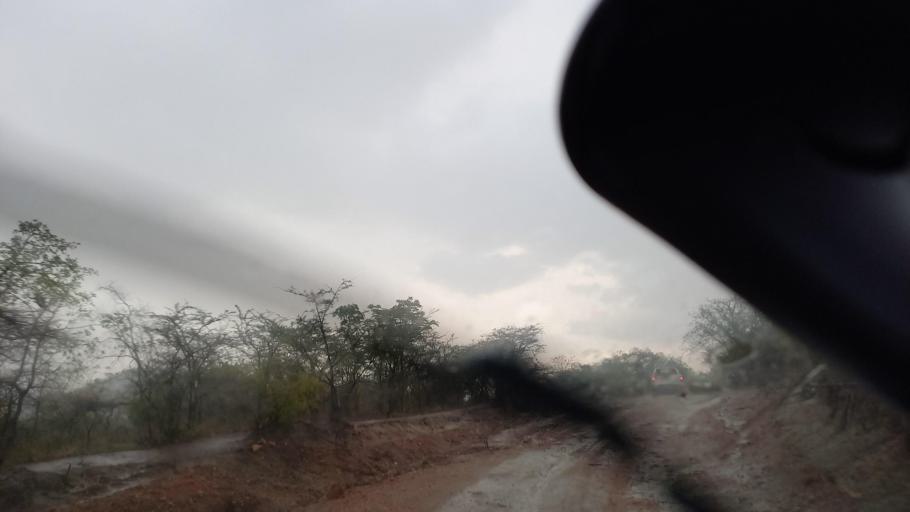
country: ZM
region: Lusaka
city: Kafue
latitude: -15.9354
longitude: 28.2102
